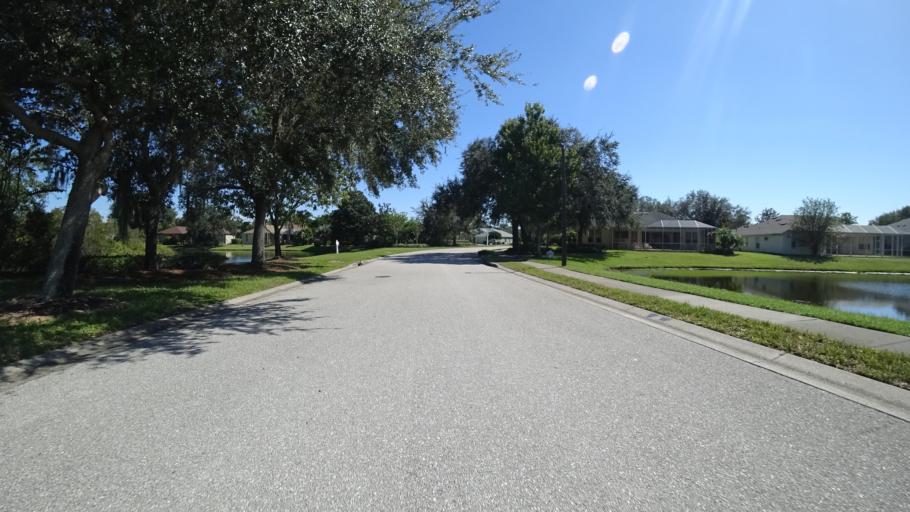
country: US
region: Florida
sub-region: Sarasota County
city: The Meadows
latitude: 27.4229
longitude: -82.4213
